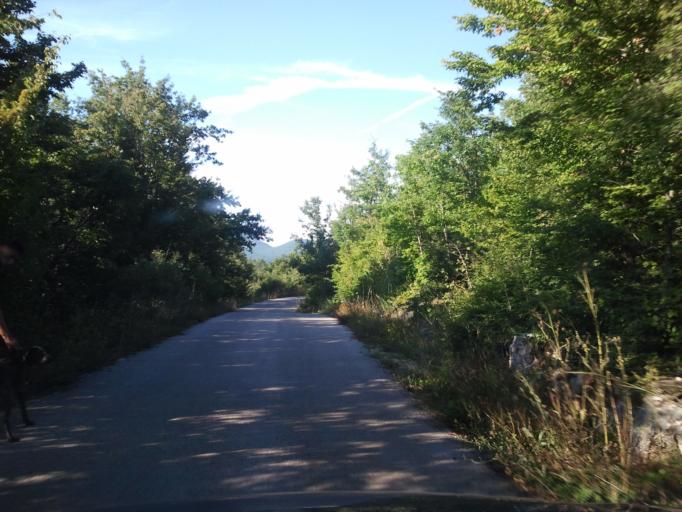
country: HR
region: Zadarska
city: Gracac
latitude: 44.3689
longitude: 15.7057
